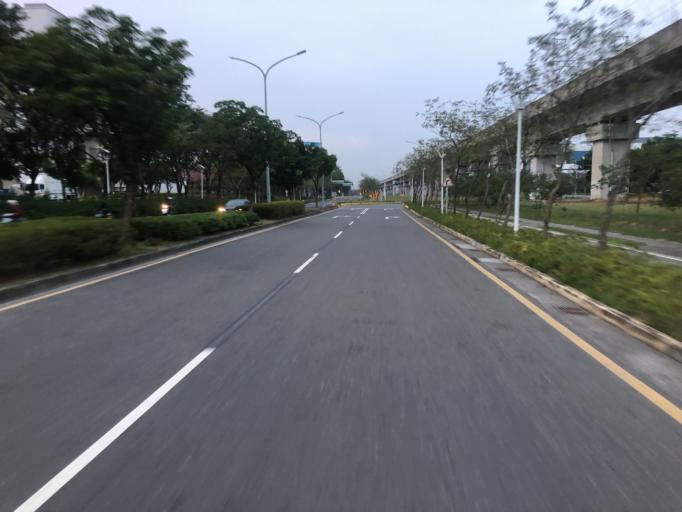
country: TW
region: Taiwan
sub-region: Tainan
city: Tainan
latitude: 23.0939
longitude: 120.2859
